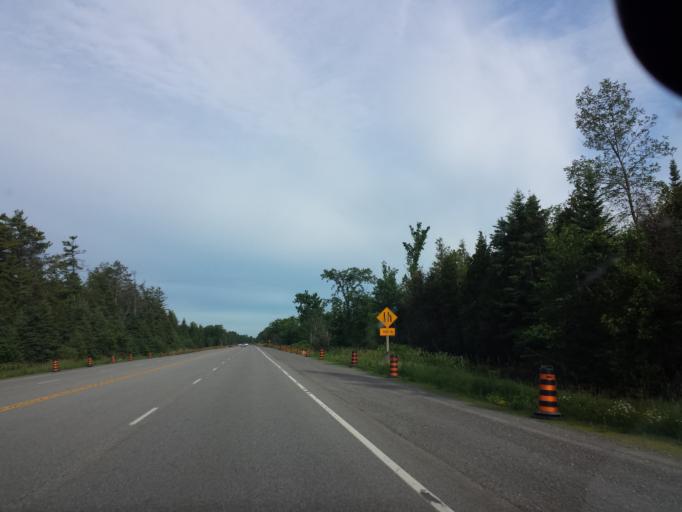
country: CA
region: Ontario
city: Arnprior
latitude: 45.4366
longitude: -76.4366
